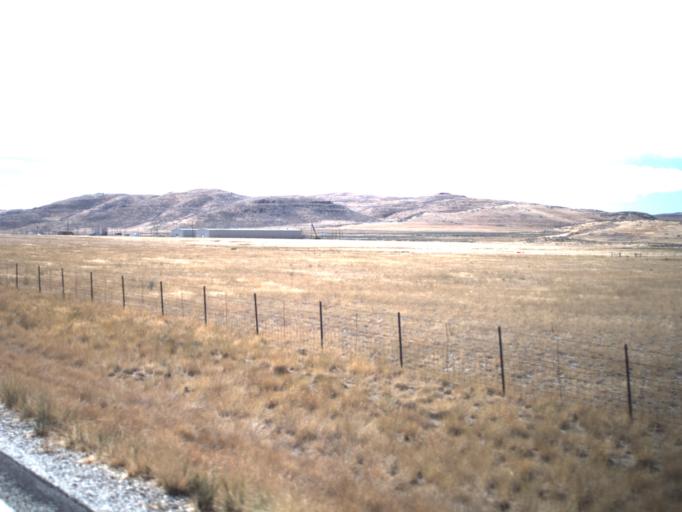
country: US
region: Utah
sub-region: Box Elder County
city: Tremonton
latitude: 41.7300
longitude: -112.4339
